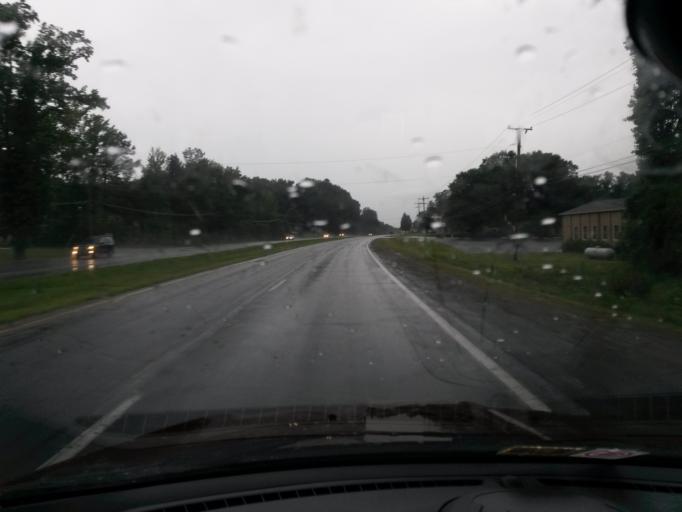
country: US
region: Virginia
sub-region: Chesterfield County
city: Enon
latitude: 37.3260
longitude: -77.3176
